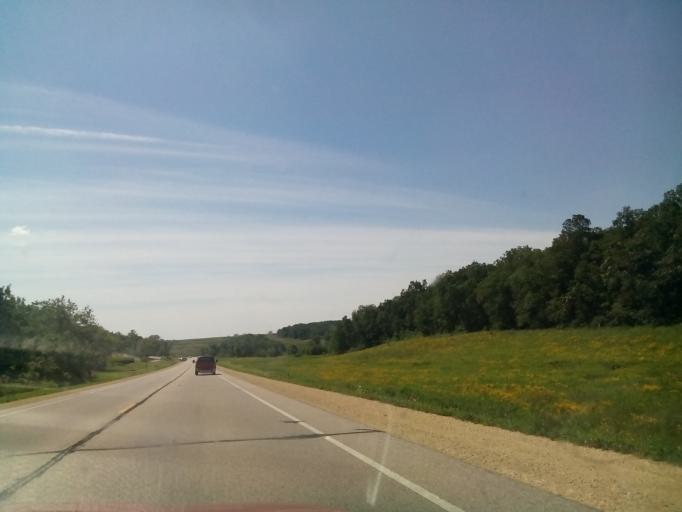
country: US
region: Wisconsin
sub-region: Green County
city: New Glarus
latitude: 42.7783
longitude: -89.6280
